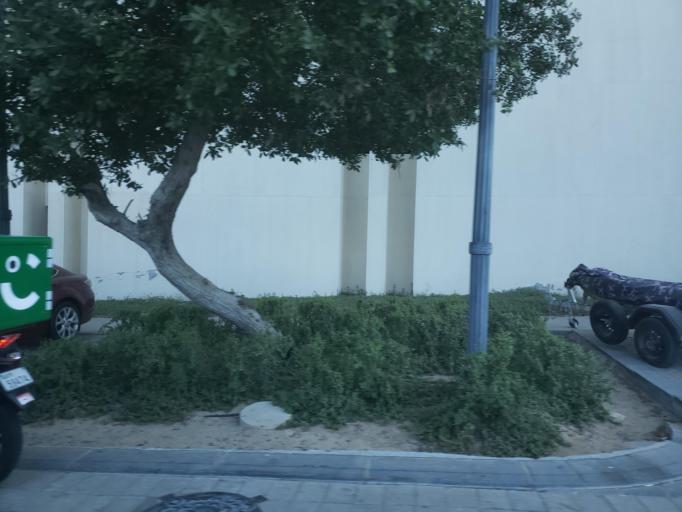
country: AE
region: Dubai
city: Dubai
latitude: 25.0482
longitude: 55.2481
